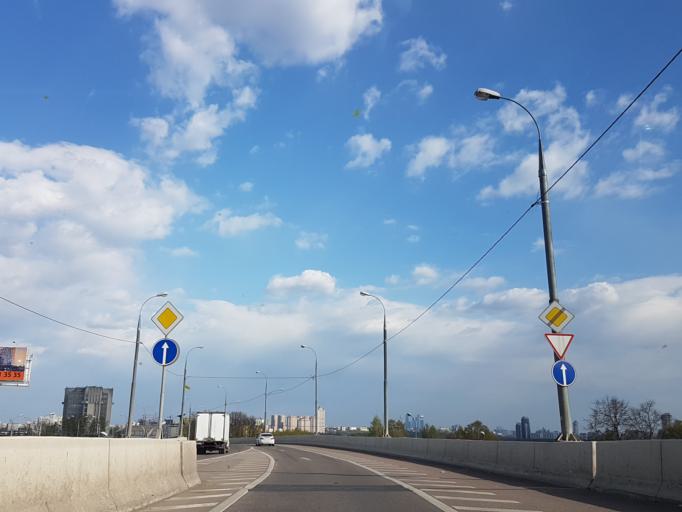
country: RU
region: Moscow
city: Strogino
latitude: 55.8333
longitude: 37.3888
